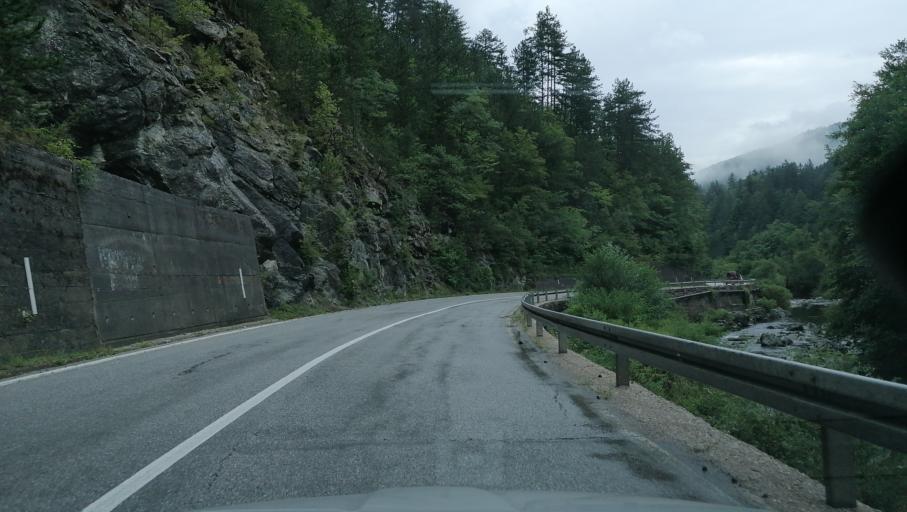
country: RS
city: Durici
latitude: 43.7757
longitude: 19.3770
